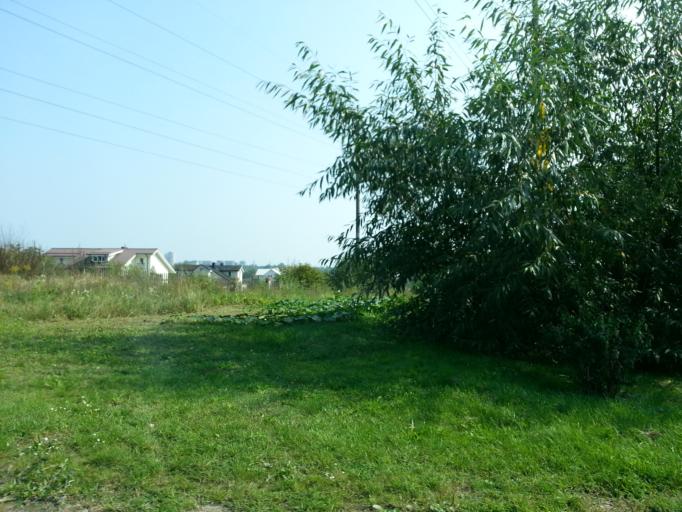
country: LT
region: Vilnius County
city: Justiniskes
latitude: 54.7262
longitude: 25.1955
